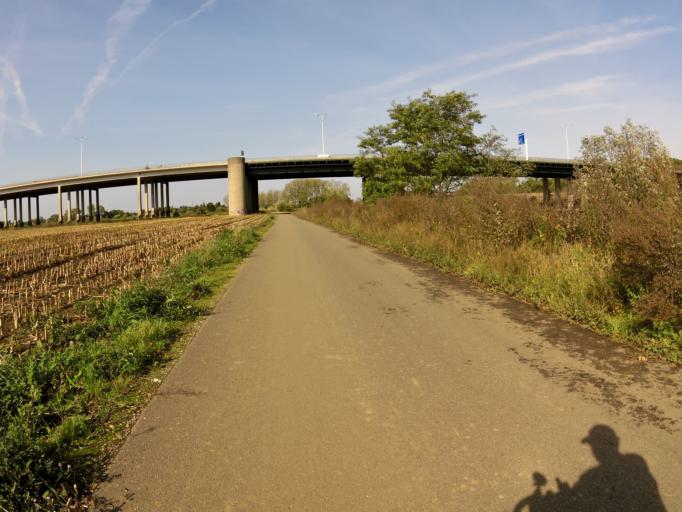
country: NL
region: Limburg
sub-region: Gemeente Stein
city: Stein
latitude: 50.9570
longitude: 5.7550
